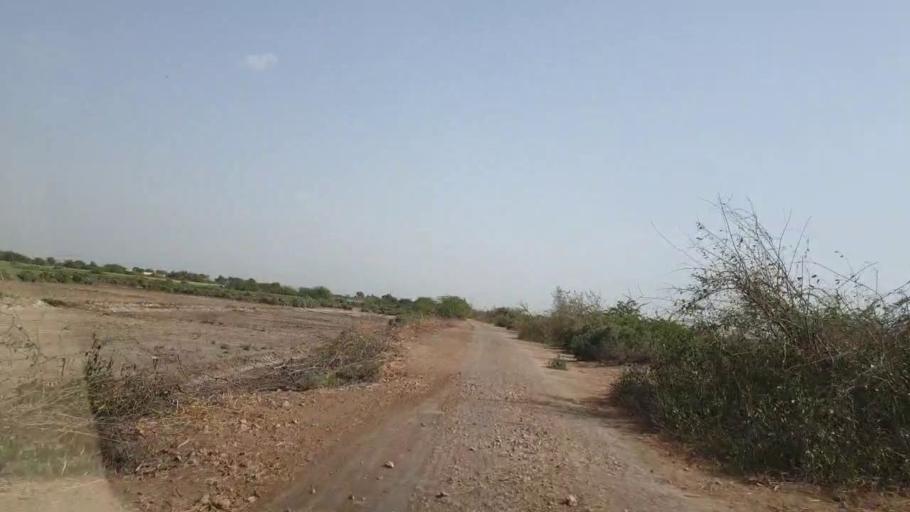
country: PK
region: Sindh
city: Rajo Khanani
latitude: 25.0457
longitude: 68.8494
